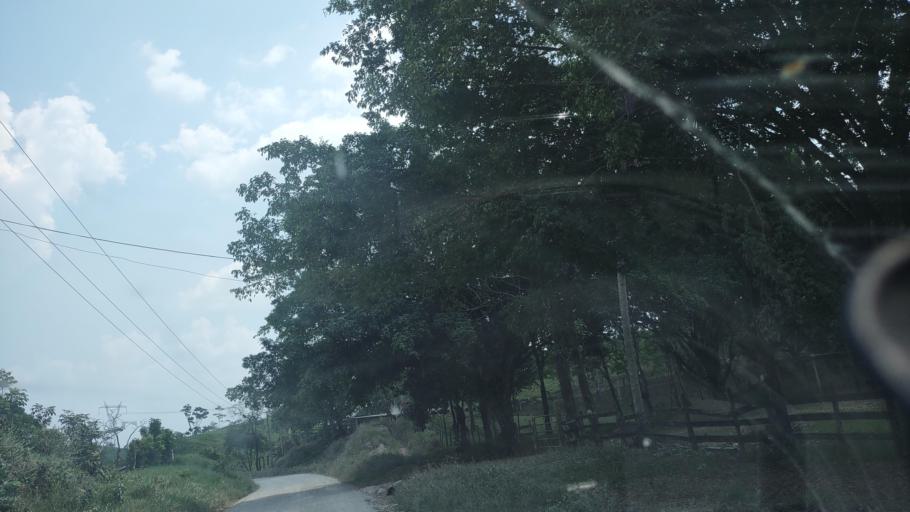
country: MX
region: Tabasco
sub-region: Huimanguillo
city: Francisco Rueda
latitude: 17.5977
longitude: -93.8998
